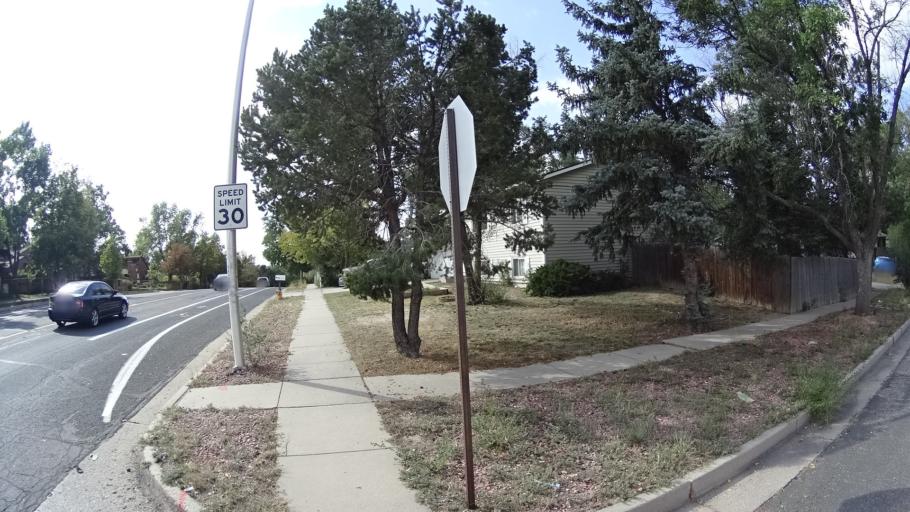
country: US
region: Colorado
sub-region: El Paso County
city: Cimarron Hills
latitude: 38.8838
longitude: -104.7387
